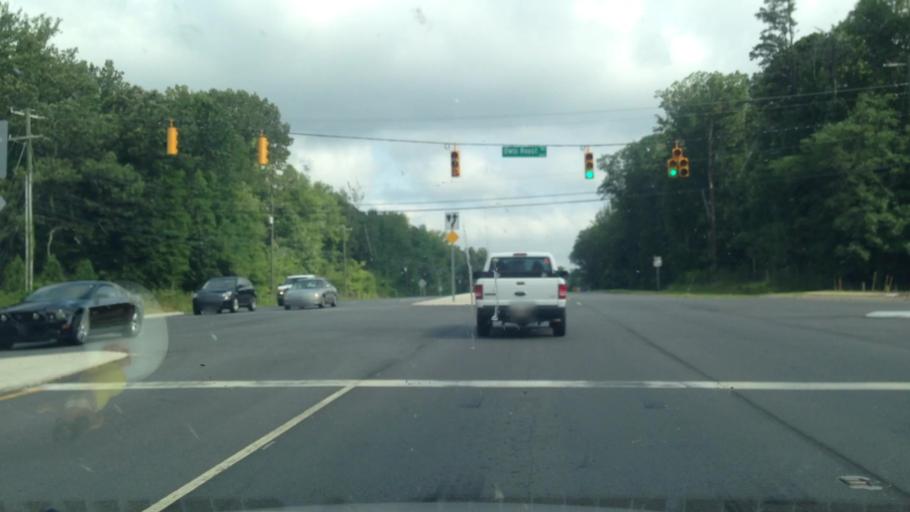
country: US
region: North Carolina
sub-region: Guilford County
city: Summerfield
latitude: 36.1602
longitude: -79.8757
